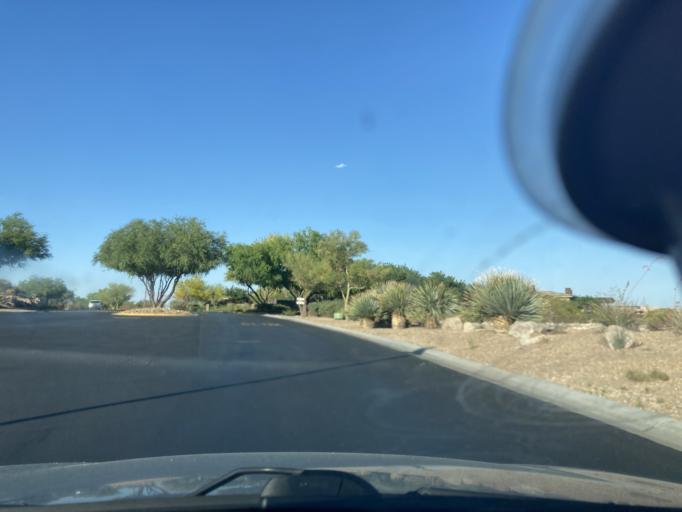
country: US
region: Nevada
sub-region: Clark County
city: Summerlin South
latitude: 36.1202
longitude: -115.3470
